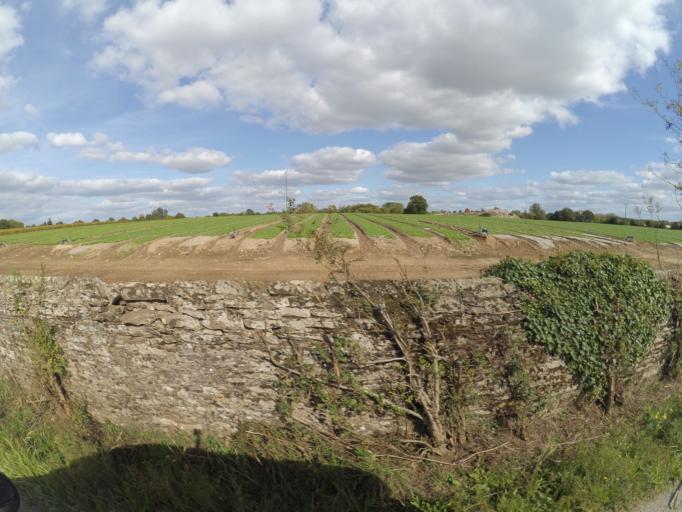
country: FR
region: Pays de la Loire
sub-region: Departement de la Loire-Atlantique
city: Saint-Julien-de-Concelles
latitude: 47.2316
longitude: -1.3791
